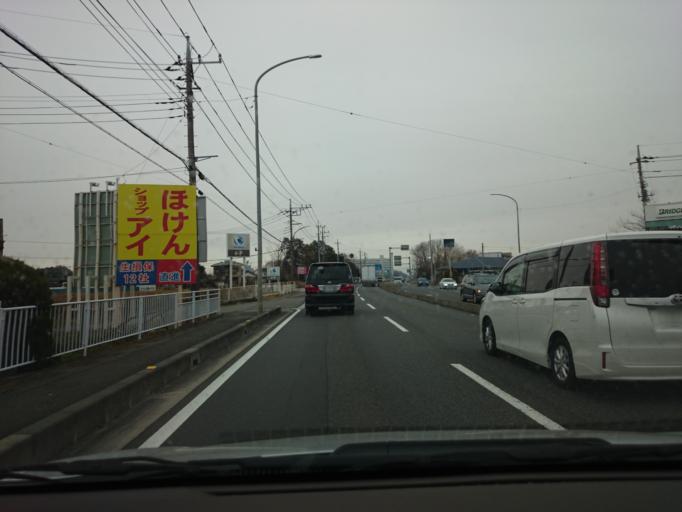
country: JP
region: Saitama
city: Hanyu
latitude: 36.1470
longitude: 139.5419
